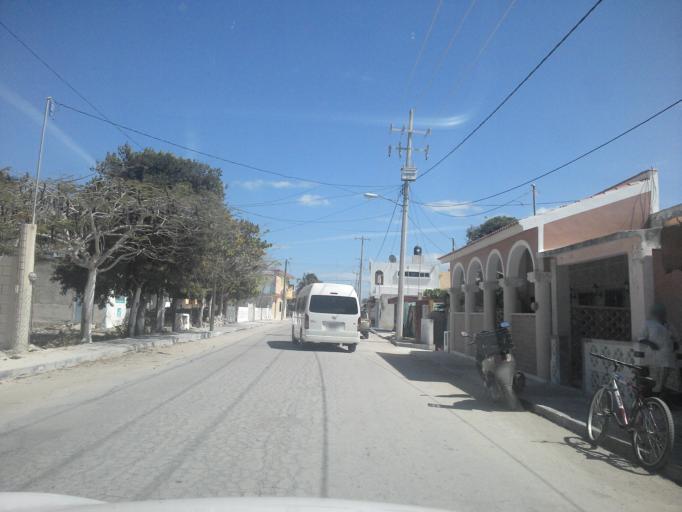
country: MX
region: Yucatan
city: Telchac Puerto
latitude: 21.3418
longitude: -89.2703
